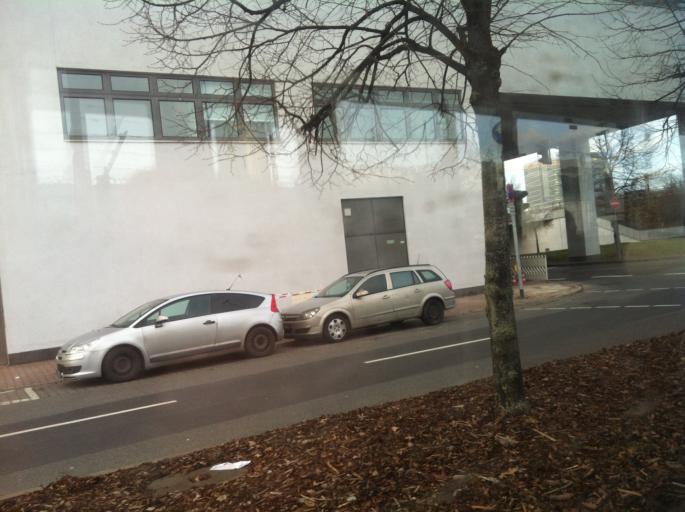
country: DE
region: Hesse
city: Niederrad
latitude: 50.0512
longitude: 8.5934
